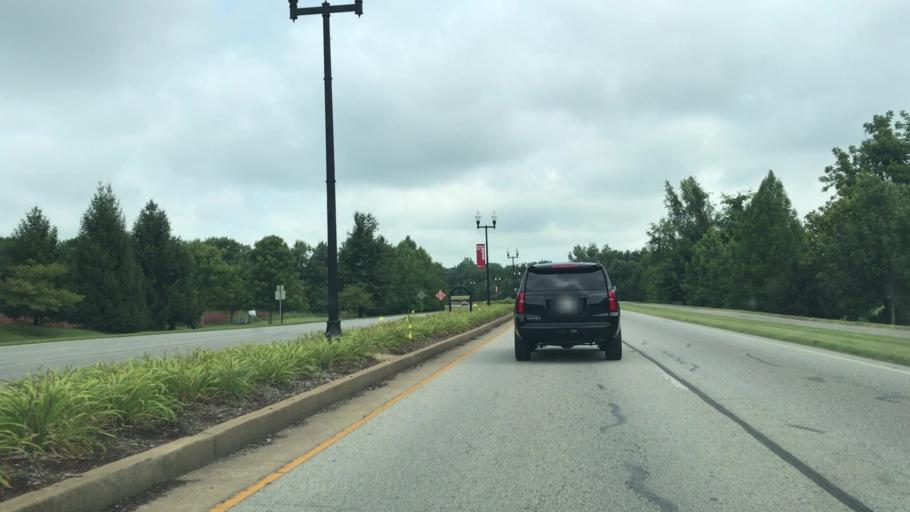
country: US
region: Kentucky
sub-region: Warren County
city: Bowling Green
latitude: 36.9821
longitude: -86.3967
